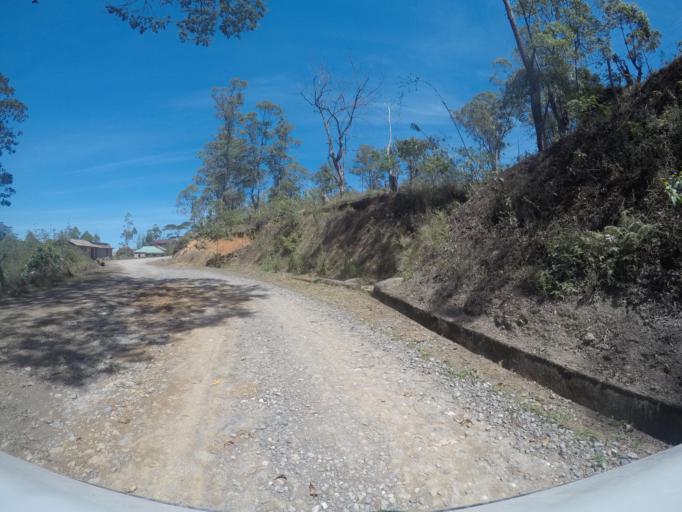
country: TL
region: Ermera
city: Gleno
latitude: -8.7852
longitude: 125.3766
